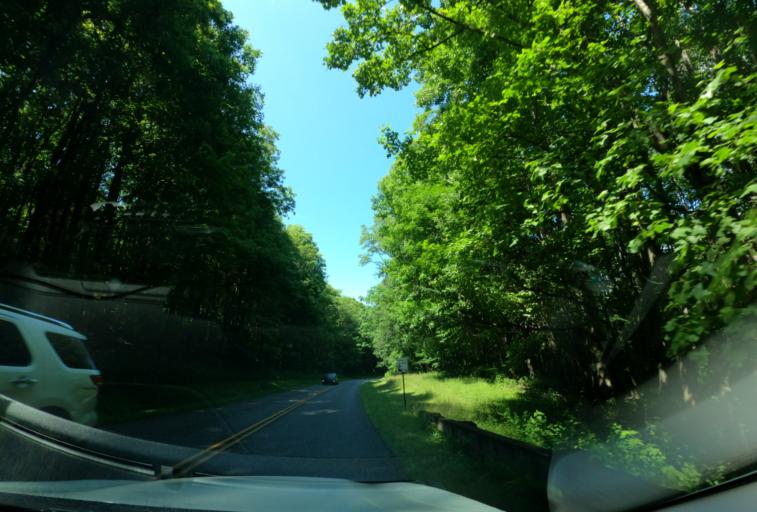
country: US
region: North Carolina
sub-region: Haywood County
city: Hazelwood
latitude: 35.4375
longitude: -83.0638
